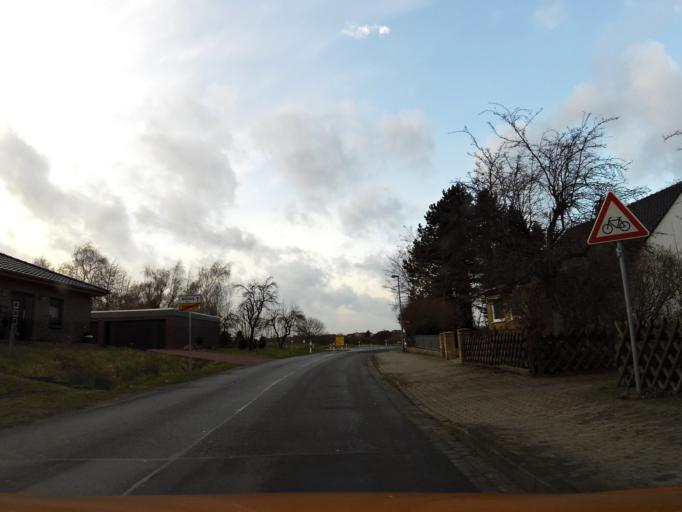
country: DE
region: Lower Saxony
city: Danndorf
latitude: 52.3929
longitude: 10.8474
